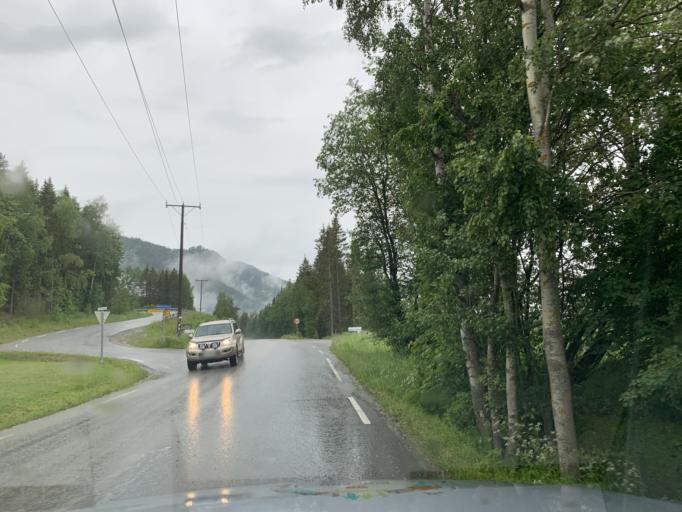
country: NO
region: Oppland
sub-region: Ringebu
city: Ringebu
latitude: 61.4479
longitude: 10.1791
